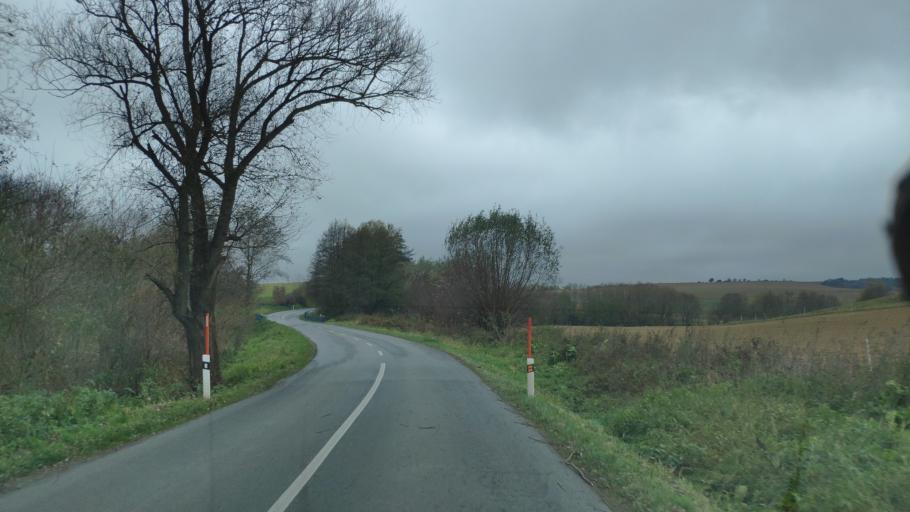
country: SK
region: Presovsky
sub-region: Okres Presov
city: Presov
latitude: 49.0983
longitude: 21.2355
